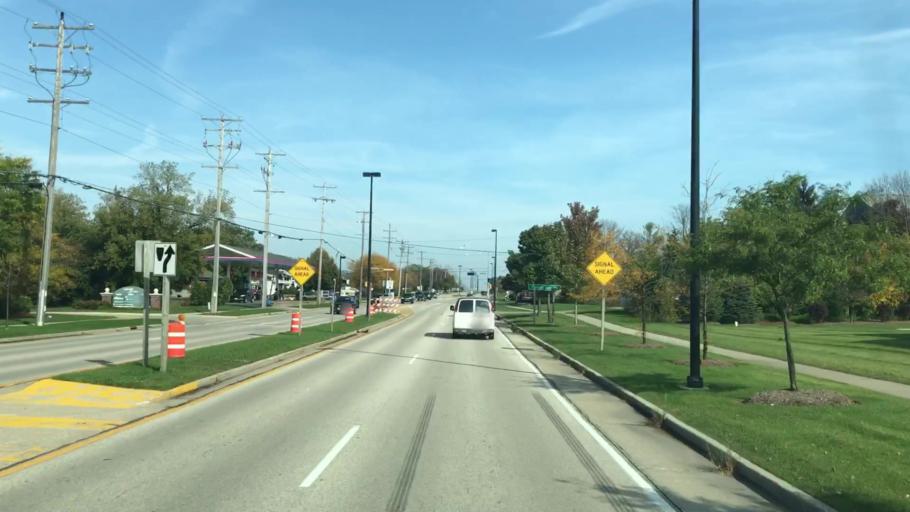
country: US
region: Wisconsin
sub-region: Milwaukee County
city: River Hills
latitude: 43.2052
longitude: -87.9242
